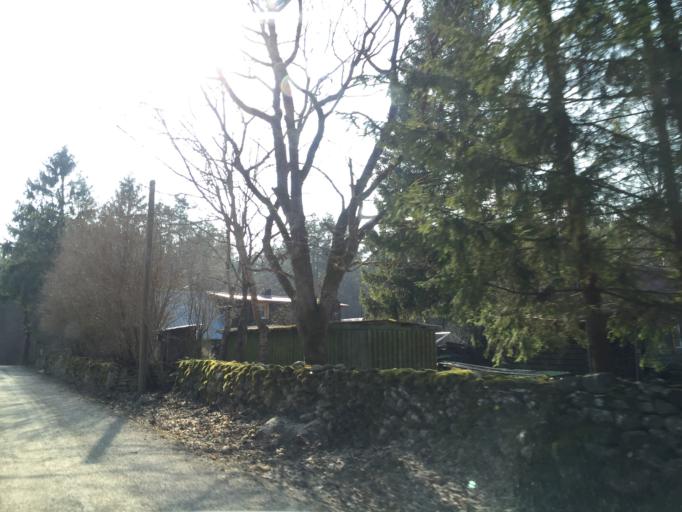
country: EE
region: Saare
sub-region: Orissaare vald
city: Orissaare
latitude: 58.5740
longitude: 23.2729
